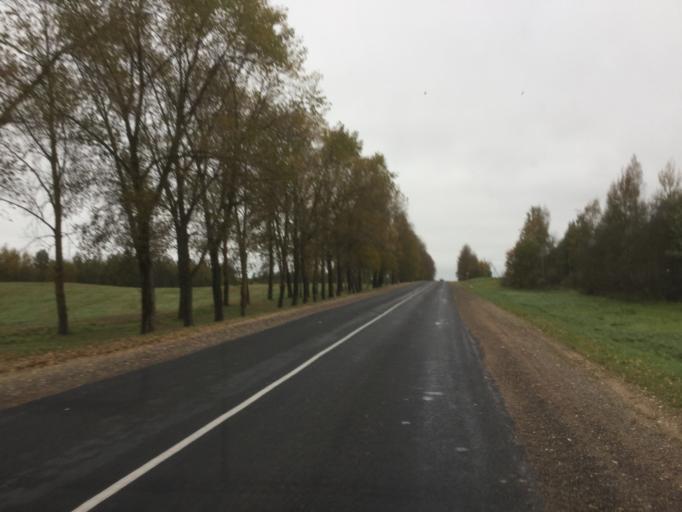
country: BY
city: Novolukoml'
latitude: 54.7330
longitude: 29.1434
